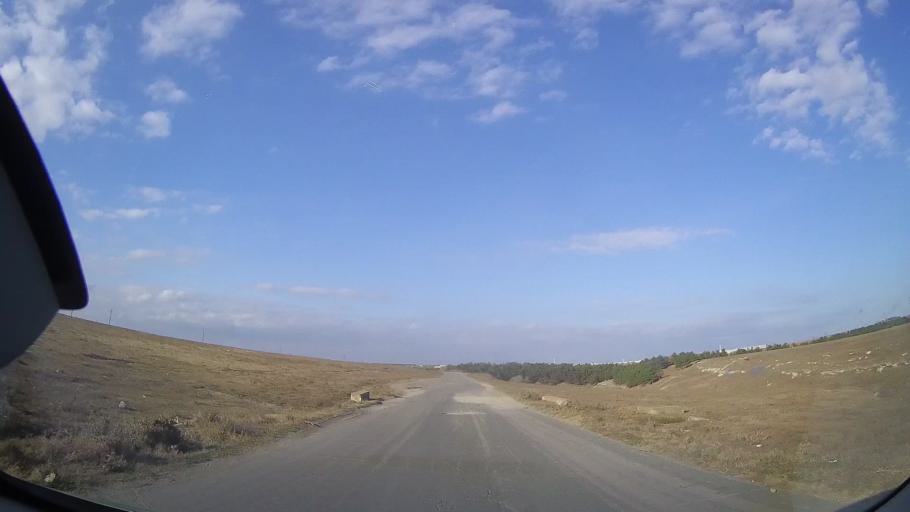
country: RO
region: Constanta
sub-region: Comuna Limanu
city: Limanu
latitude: 43.8061
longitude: 28.5203
